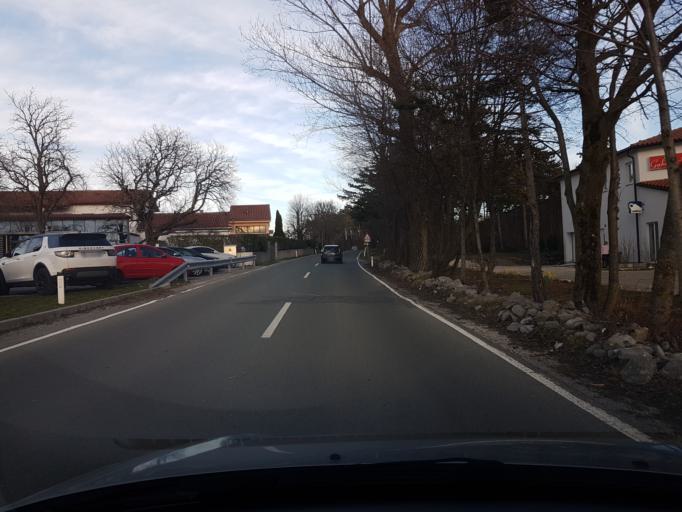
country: SI
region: Sezana
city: Sezana
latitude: 45.6576
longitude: 13.8927
